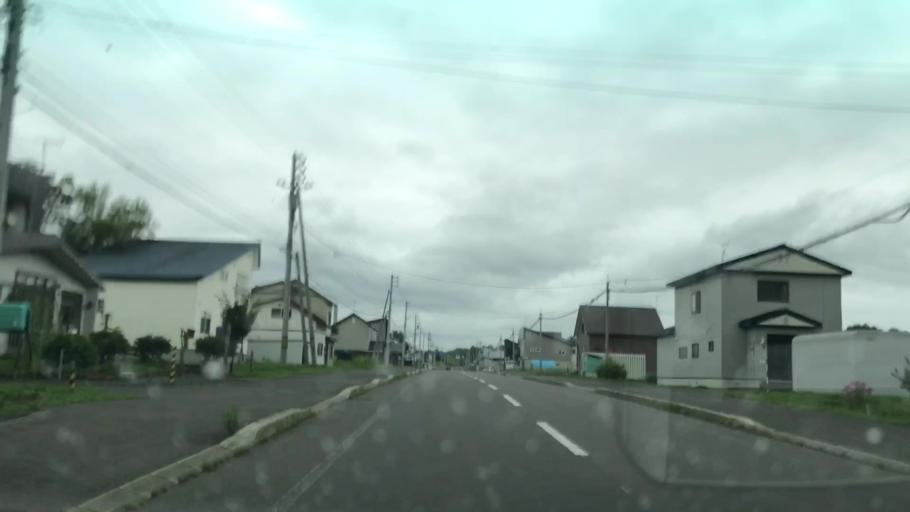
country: JP
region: Hokkaido
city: Niseko Town
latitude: 42.7976
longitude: 140.7073
